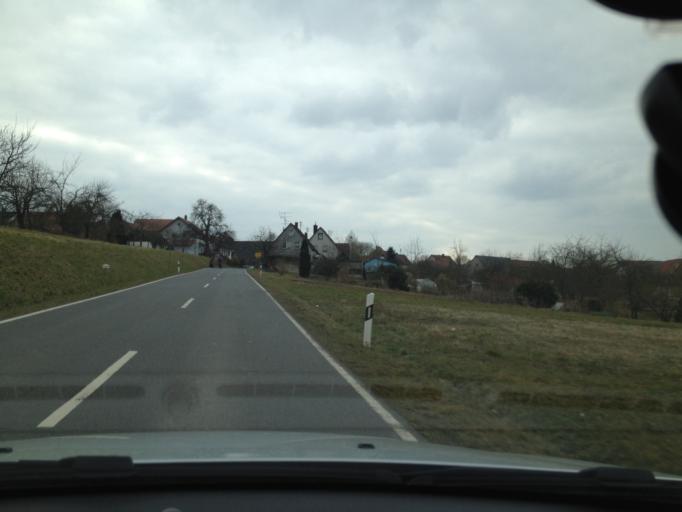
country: DE
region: Baden-Wuerttemberg
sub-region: Regierungsbezirk Stuttgart
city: Wertheim
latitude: 49.7315
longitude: 9.4973
